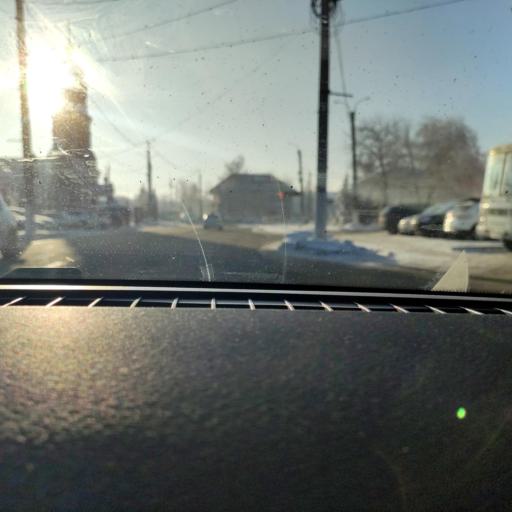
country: RU
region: Samara
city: Novokuybyshevsk
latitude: 53.1037
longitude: 49.9542
